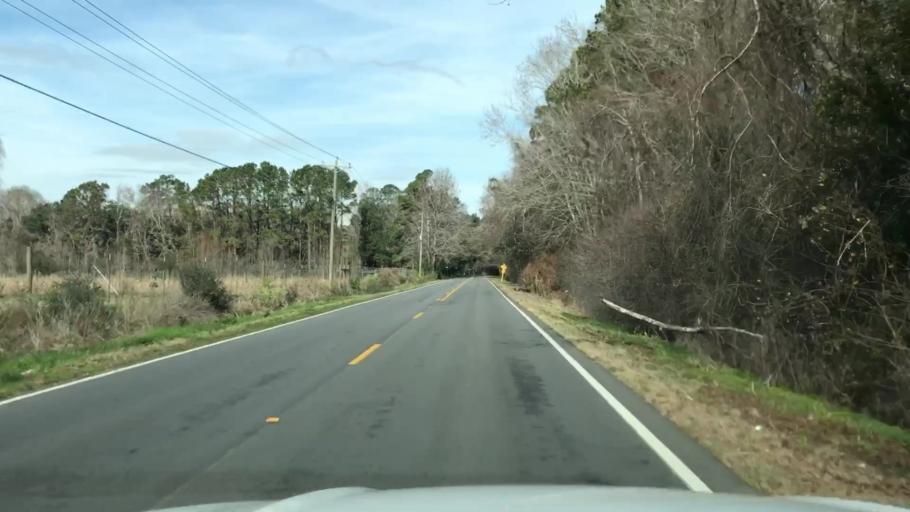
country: US
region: South Carolina
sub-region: Charleston County
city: Charleston
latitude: 32.7231
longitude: -80.0229
